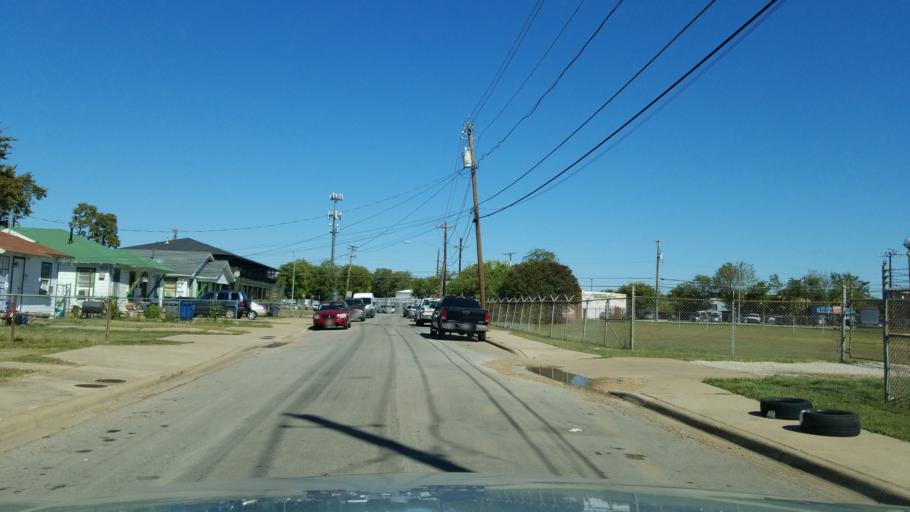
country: US
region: Texas
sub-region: Dallas County
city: Dallas
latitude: 32.7820
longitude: -96.7465
